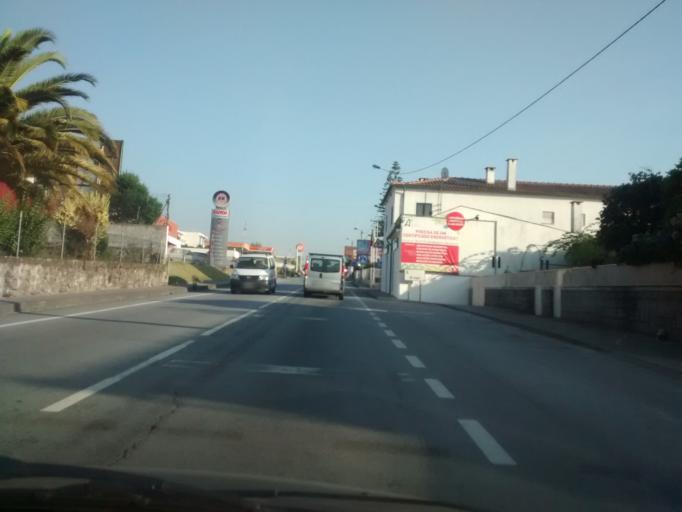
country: PT
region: Braga
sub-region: Braga
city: Braga
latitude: 41.5783
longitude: -8.4265
